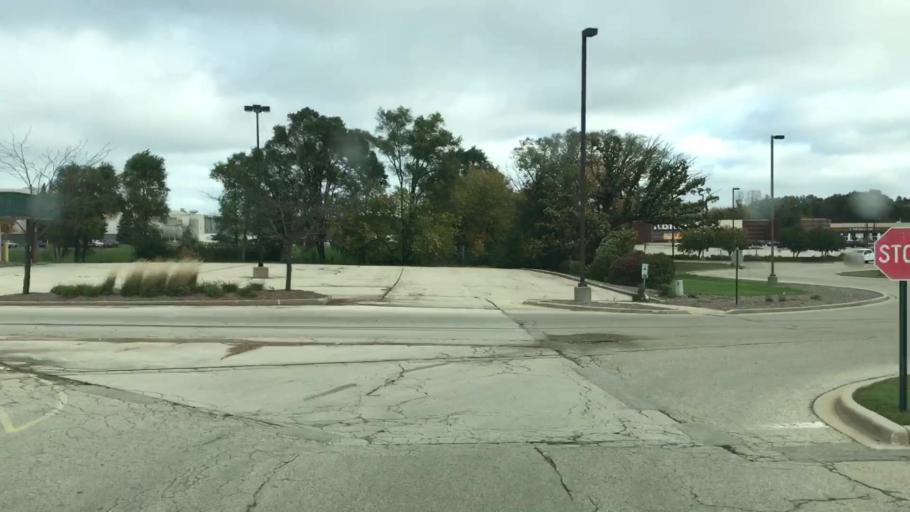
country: US
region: Wisconsin
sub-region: Waukesha County
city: Waukesha
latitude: 42.9897
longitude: -88.2673
